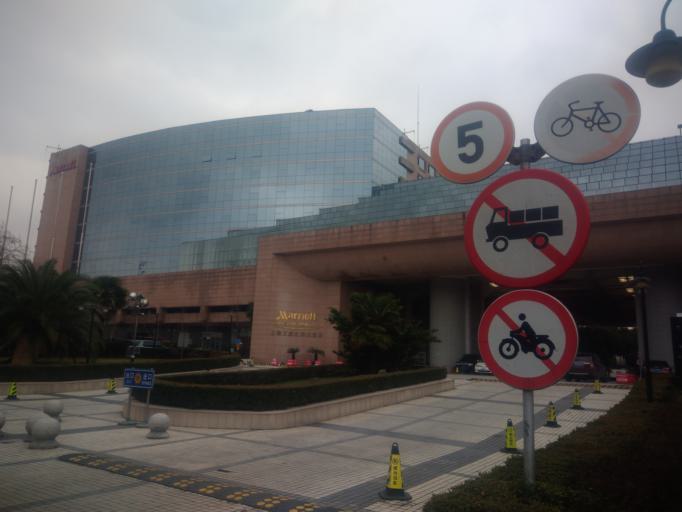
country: CN
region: Shanghai Shi
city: Changzheng
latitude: 31.1938
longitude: 121.3714
